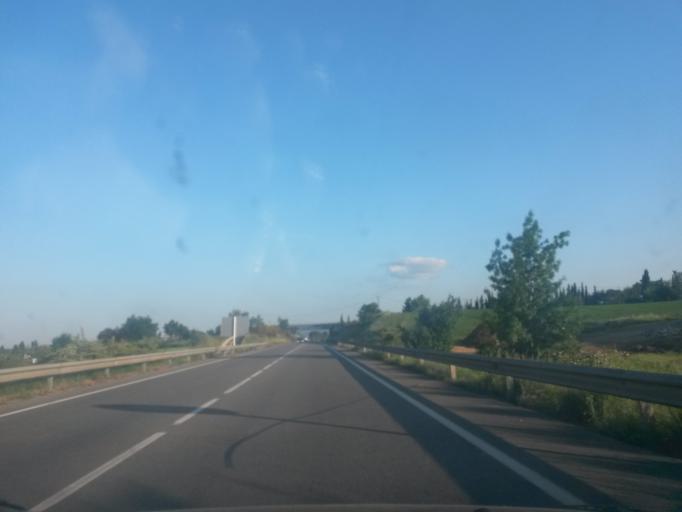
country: ES
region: Catalonia
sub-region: Provincia de Girona
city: Fontcoberta
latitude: 42.1189
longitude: 2.7873
